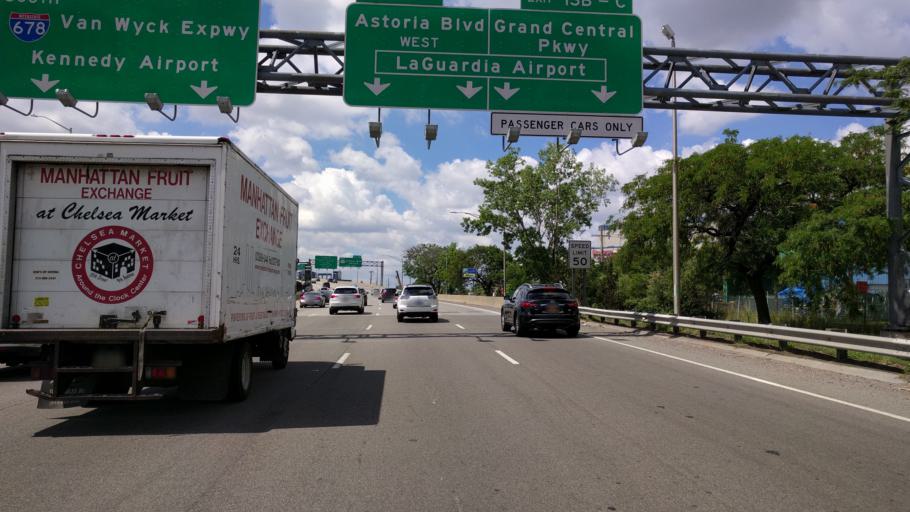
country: US
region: New York
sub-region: Queens County
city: Jamaica
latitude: 40.7690
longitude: -73.8371
